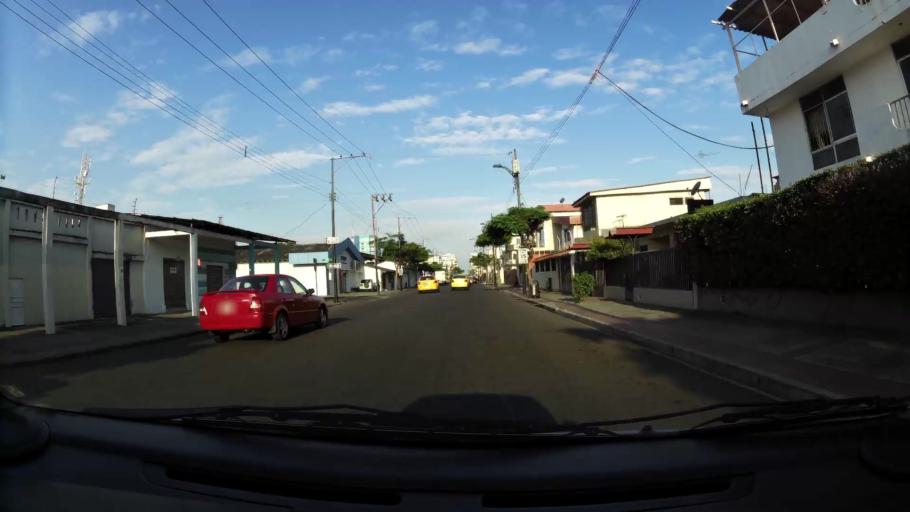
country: EC
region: Guayas
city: Guayaquil
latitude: -2.2145
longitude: -79.8927
